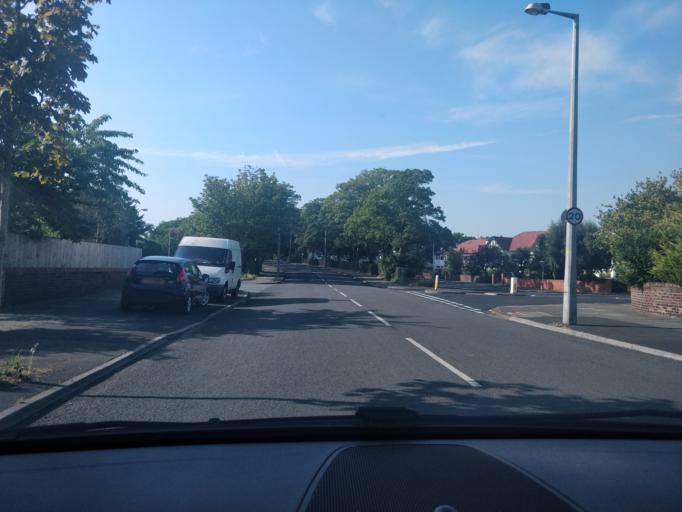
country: GB
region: England
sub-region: Sefton
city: Southport
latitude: 53.6558
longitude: -2.9749
